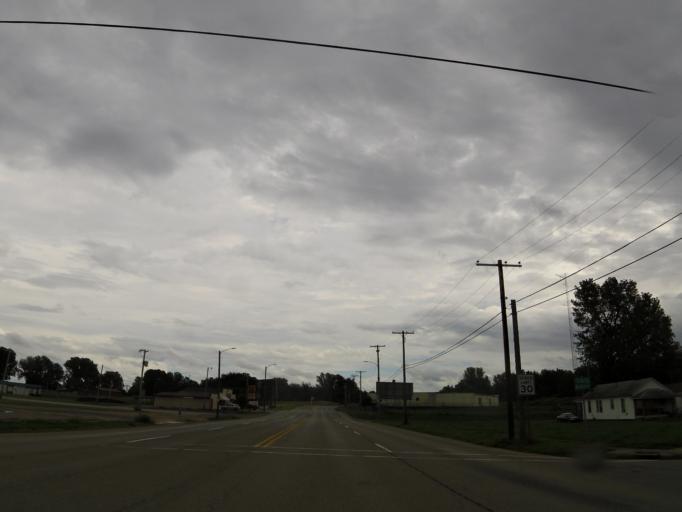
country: US
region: Illinois
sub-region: Alexander County
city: Cairo
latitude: 36.9978
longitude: -89.1641
